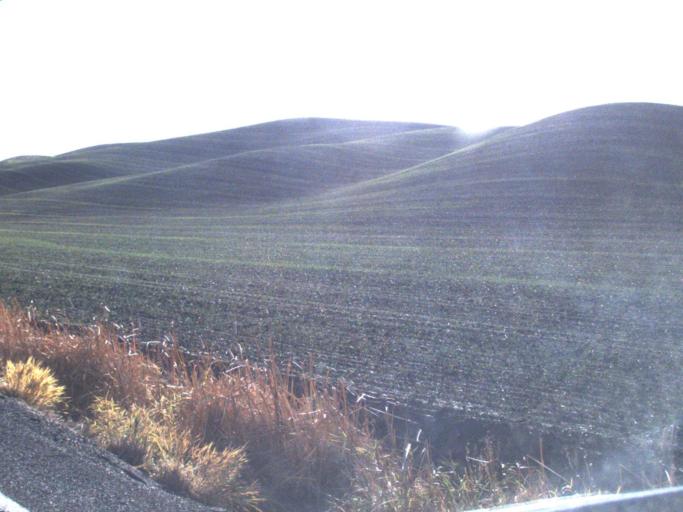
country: US
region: Washington
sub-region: Whitman County
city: Colfax
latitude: 46.7506
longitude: -117.3705
